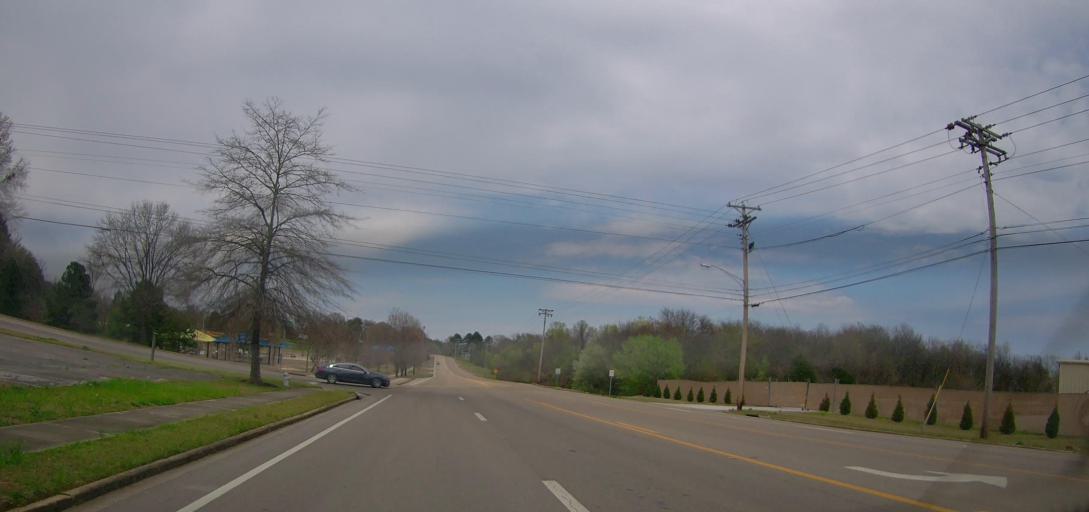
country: US
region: Mississippi
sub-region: Lee County
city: Tupelo
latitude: 34.2644
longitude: -88.7036
